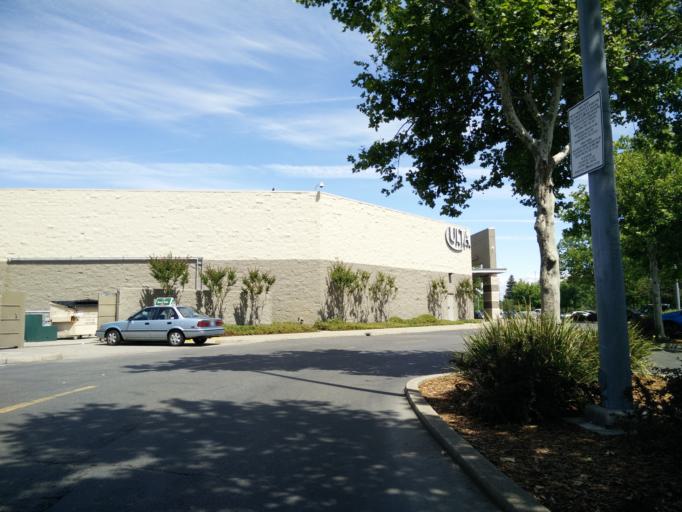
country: US
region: California
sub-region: Shasta County
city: Redding
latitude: 40.5873
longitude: -122.3563
